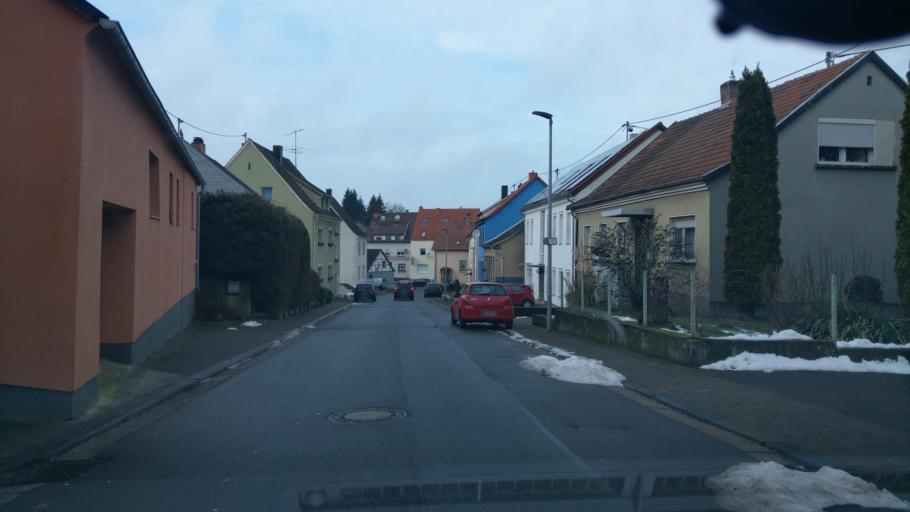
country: DE
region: Saarland
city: Hangard
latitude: 49.3683
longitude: 7.1913
